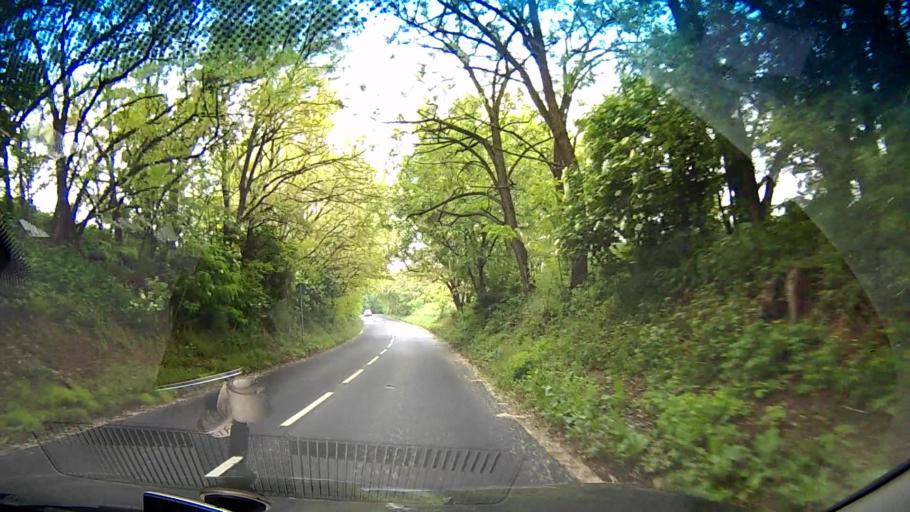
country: HU
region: Pest
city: Perbal
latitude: 47.6311
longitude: 18.7808
